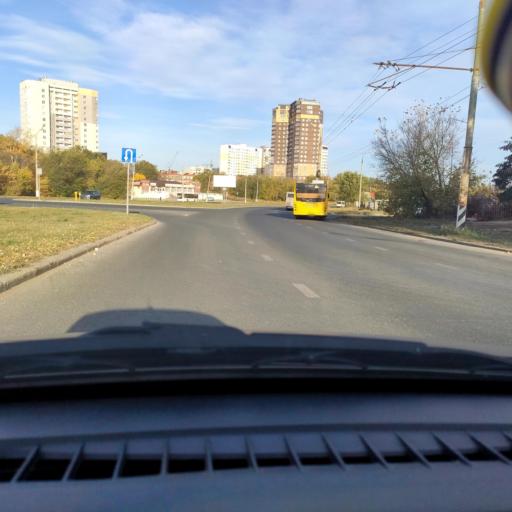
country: RU
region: Samara
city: Tol'yatti
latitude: 53.5046
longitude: 49.2568
